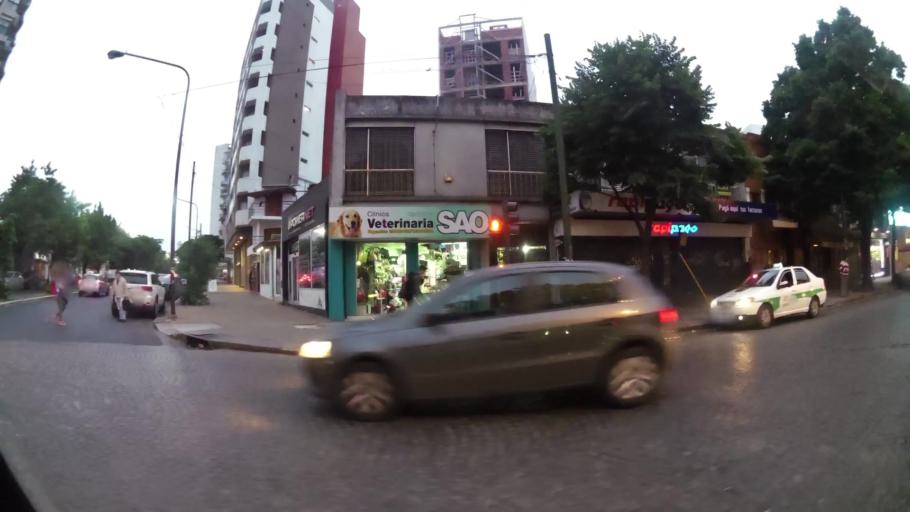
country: AR
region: Buenos Aires
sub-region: Partido de La Plata
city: La Plata
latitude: -34.9098
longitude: -57.9553
